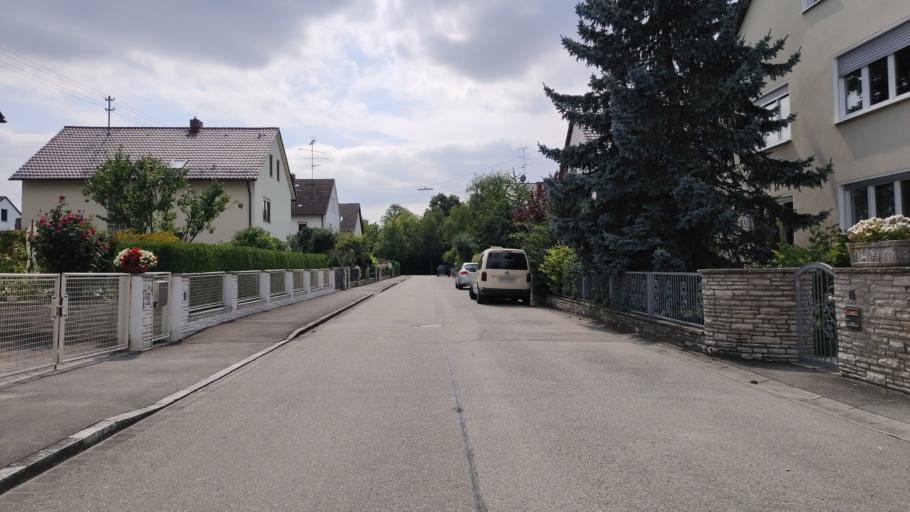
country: DE
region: Bavaria
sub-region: Swabia
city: Konigsbrunn
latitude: 48.2735
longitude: 10.8943
